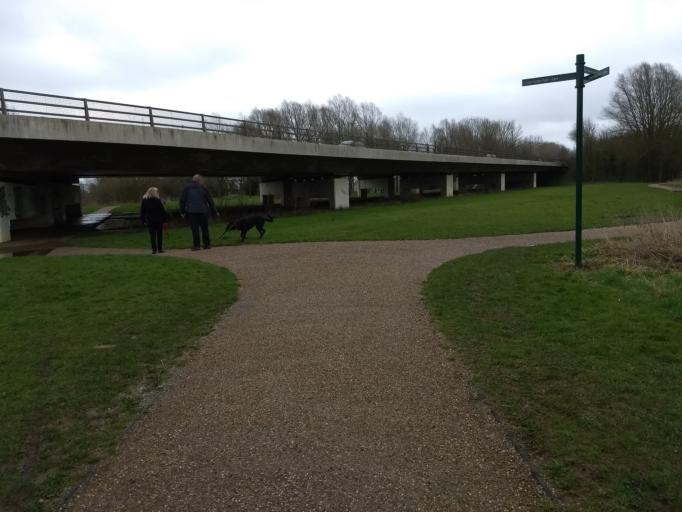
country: GB
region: England
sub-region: Milton Keynes
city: Stony Stratford
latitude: 52.0641
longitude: -0.8534
